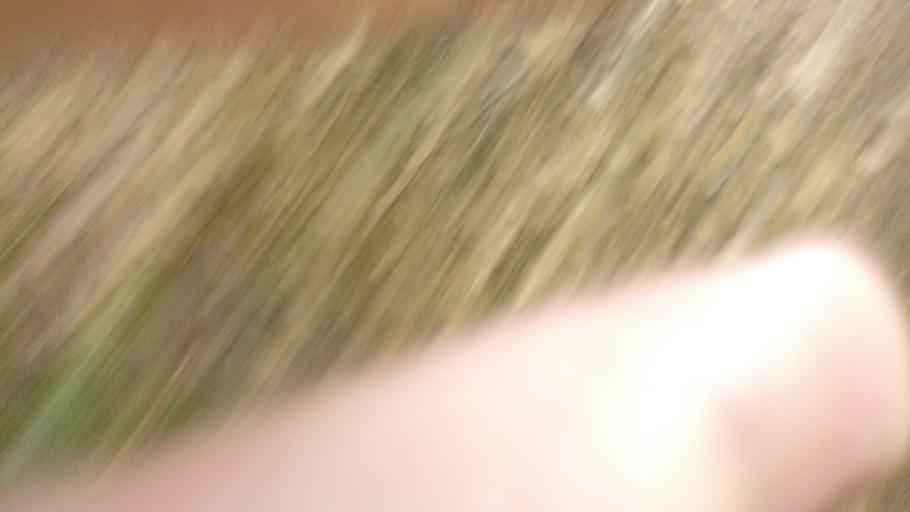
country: DE
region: Rheinland-Pfalz
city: Gemunden
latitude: 50.5640
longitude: 8.0323
